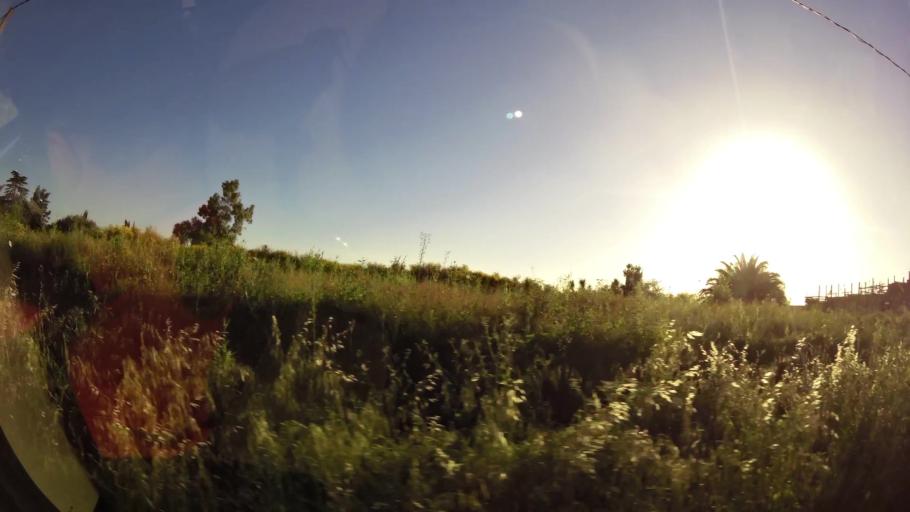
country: UY
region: Canelones
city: La Paz
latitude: -34.8314
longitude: -56.2339
